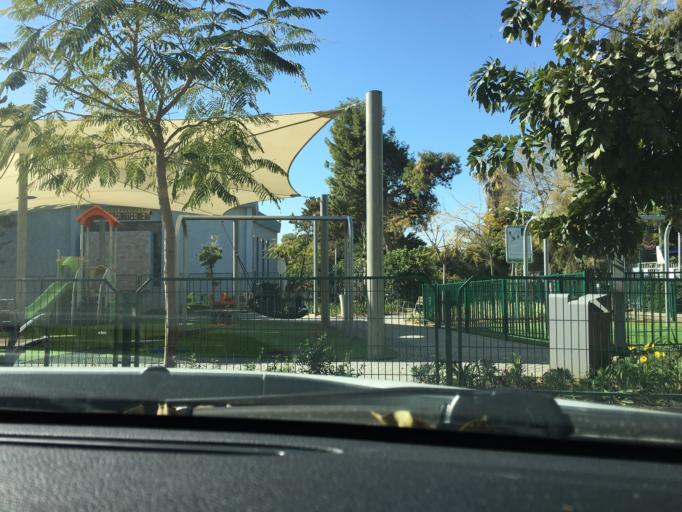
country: IL
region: Tel Aviv
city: Ramat HaSharon
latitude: 32.1490
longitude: 34.8306
